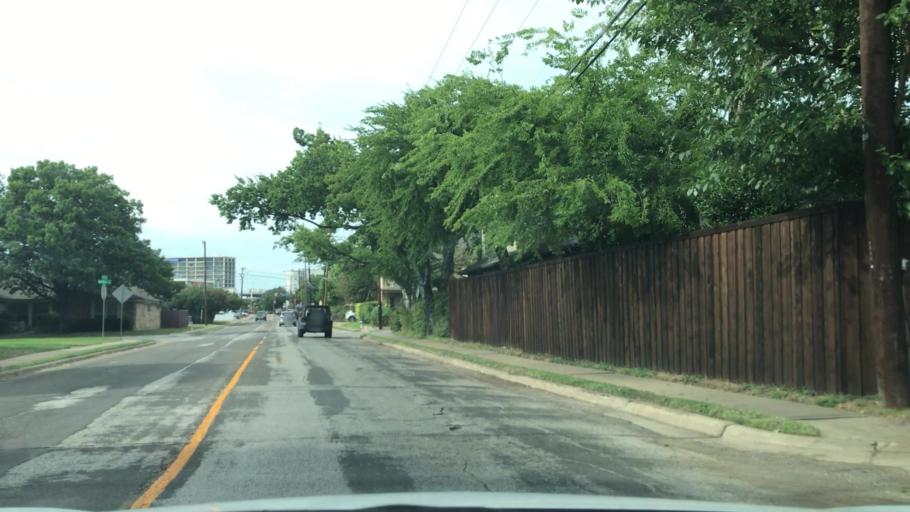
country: US
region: Texas
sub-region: Dallas County
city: Highland Park
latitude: 32.8341
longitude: -96.7738
